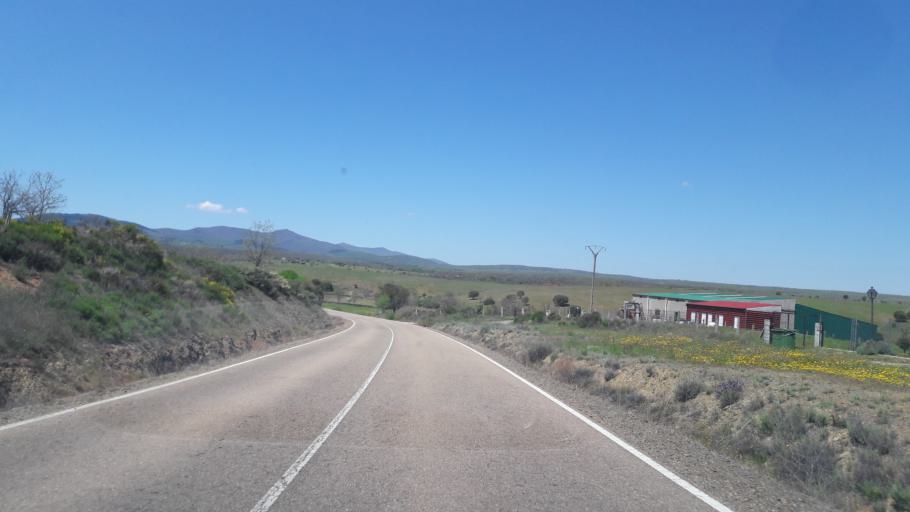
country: ES
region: Castille and Leon
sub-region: Provincia de Salamanca
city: Monleon
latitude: 40.5912
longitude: -5.8288
